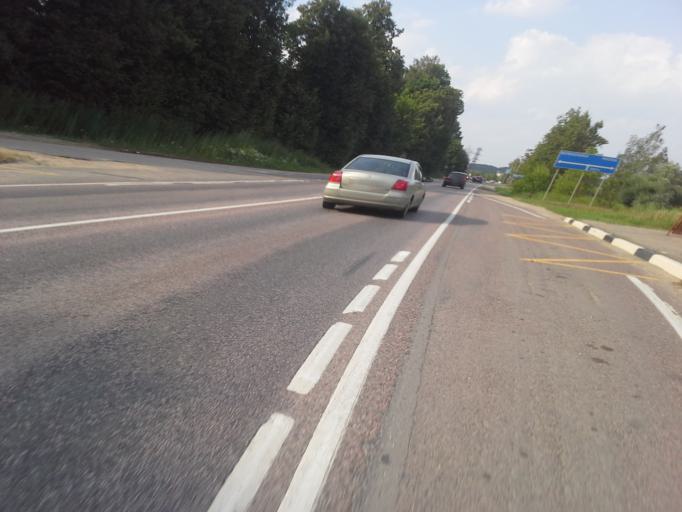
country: RU
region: Moskovskaya
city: Istra
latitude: 55.9039
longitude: 36.8081
